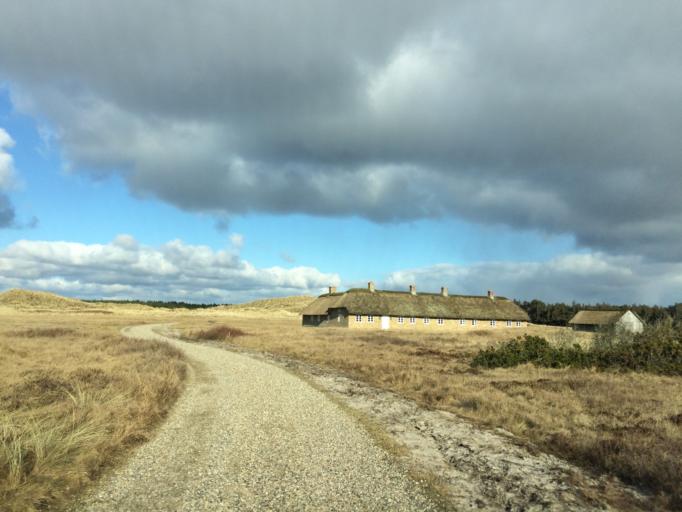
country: DK
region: Central Jutland
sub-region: Holstebro Kommune
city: Ulfborg
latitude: 56.2798
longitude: 8.1363
